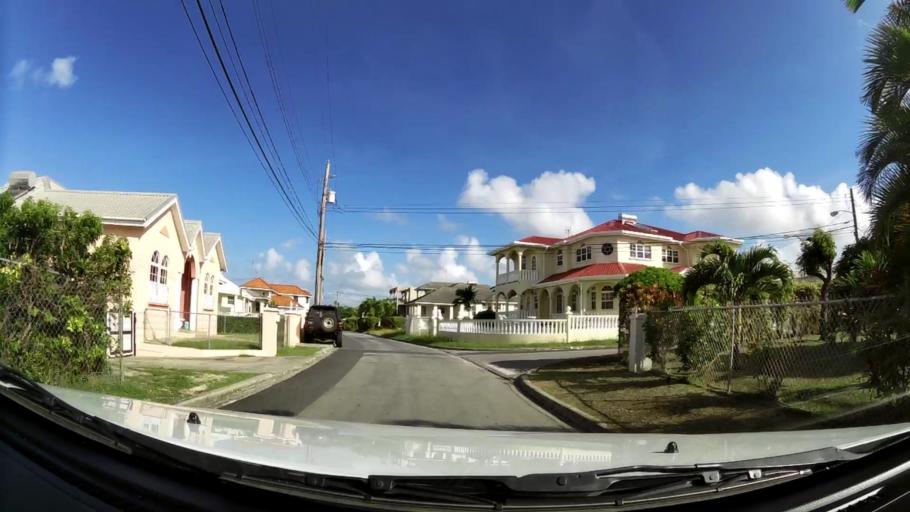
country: BB
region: Saint James
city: Holetown
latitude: 13.1529
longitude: -59.6104
